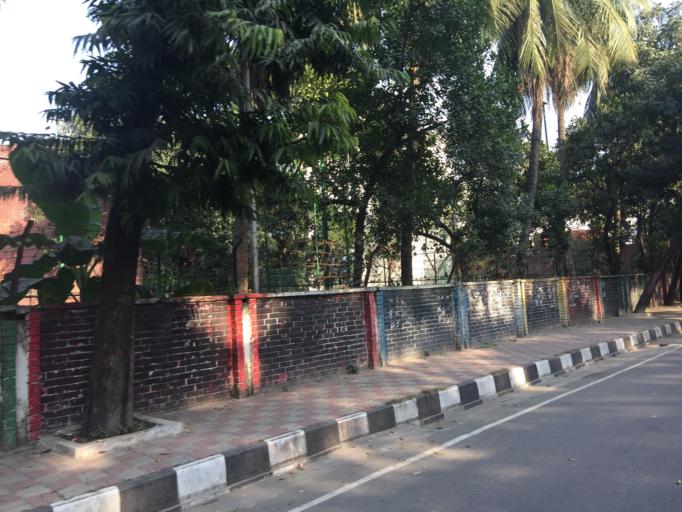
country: BD
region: Dhaka
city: Azimpur
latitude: 23.7270
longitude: 90.3903
